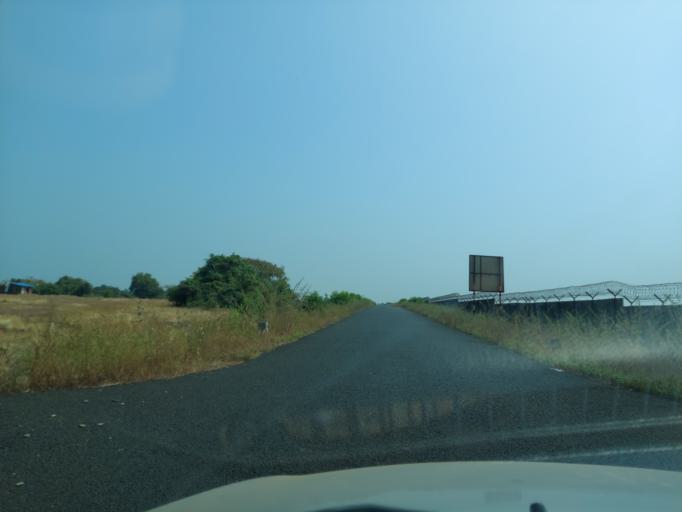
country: IN
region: Maharashtra
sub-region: Sindhudurg
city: Malvan
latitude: 16.0026
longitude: 73.5089
